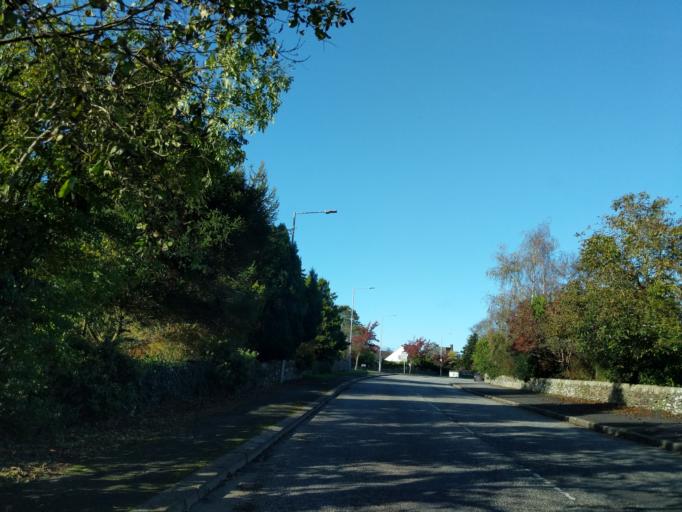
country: GB
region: Scotland
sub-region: Dumfries and Galloway
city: Kirkcudbright
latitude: 54.8320
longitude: -4.0521
